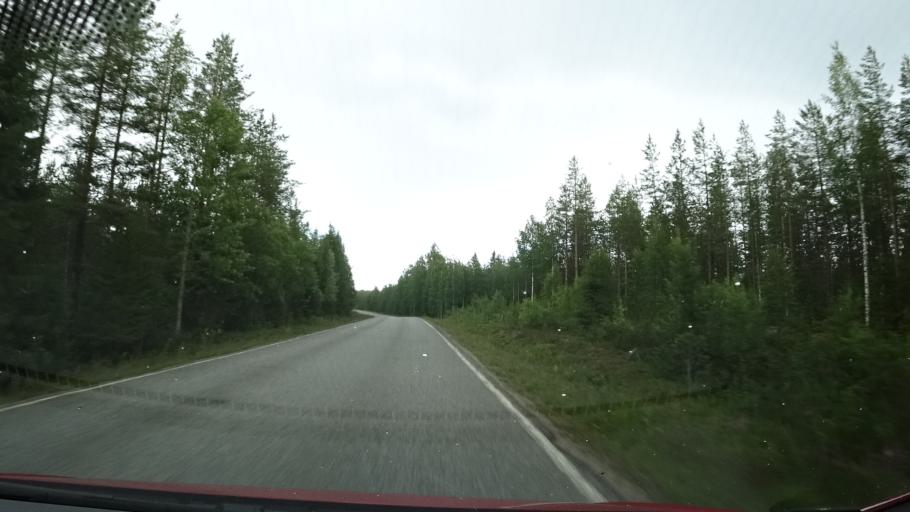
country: FI
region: Kainuu
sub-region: Kehys-Kainuu
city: Kuhmo
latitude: 63.9577
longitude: 29.2579
